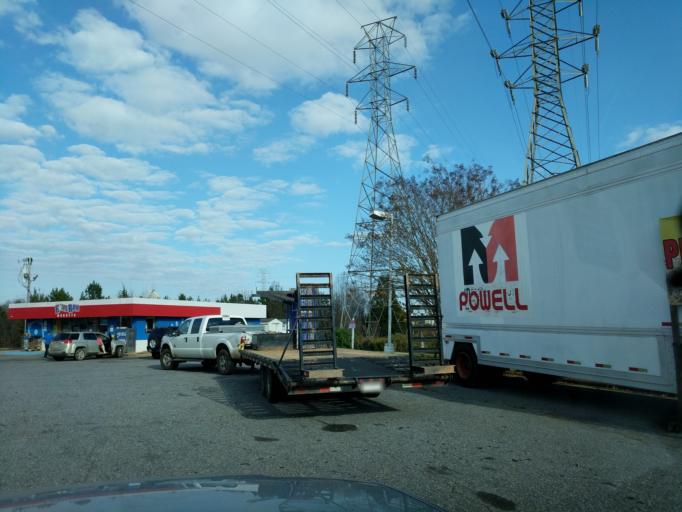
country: US
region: North Carolina
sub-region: Alexander County
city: Stony Point
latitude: 35.7720
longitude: -80.9970
